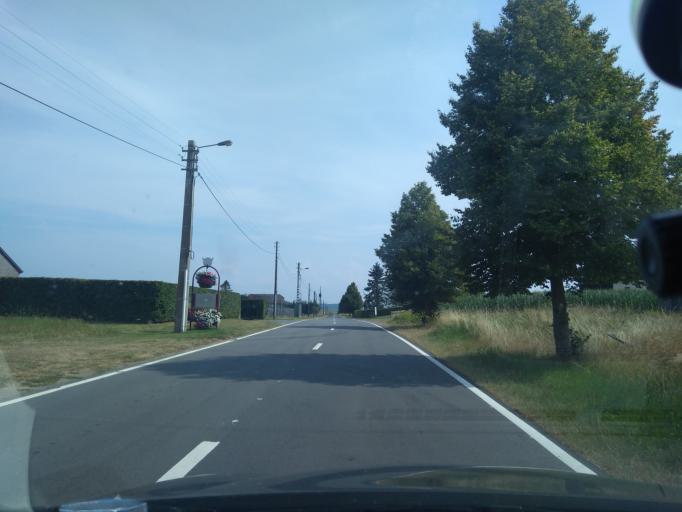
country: BE
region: Wallonia
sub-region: Province du Luxembourg
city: Bertogne
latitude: 50.1552
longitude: 5.6875
